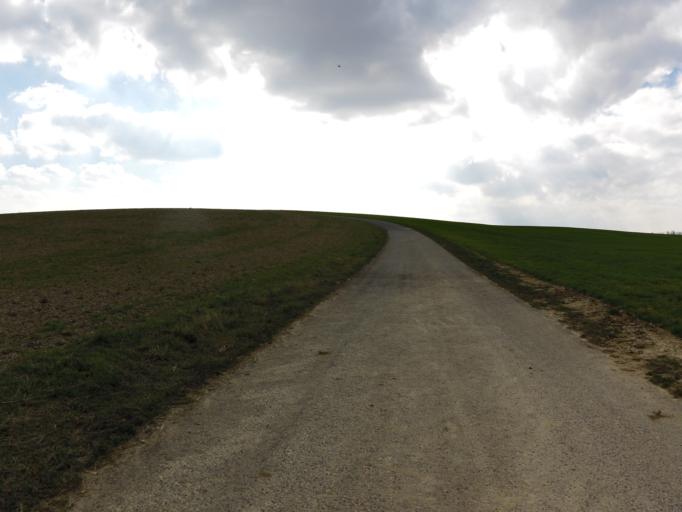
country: DE
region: Bavaria
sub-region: Regierungsbezirk Unterfranken
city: Buchbrunn
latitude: 49.7520
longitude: 10.1138
